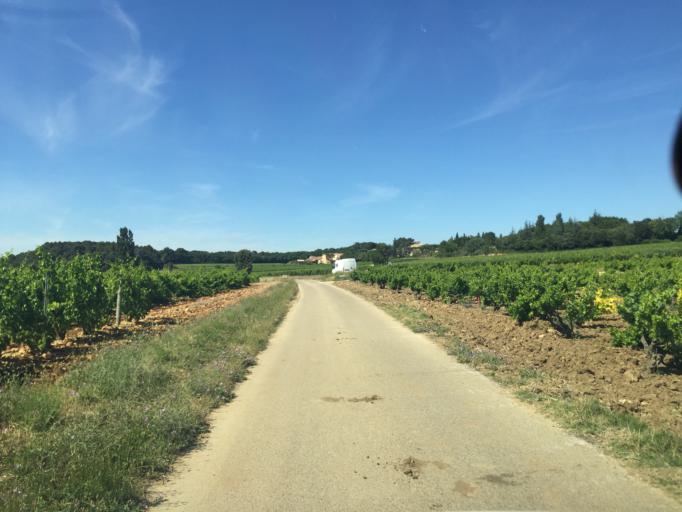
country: FR
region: Provence-Alpes-Cote d'Azur
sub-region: Departement du Vaucluse
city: Chateauneuf-du-Pape
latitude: 44.0774
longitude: 4.8078
